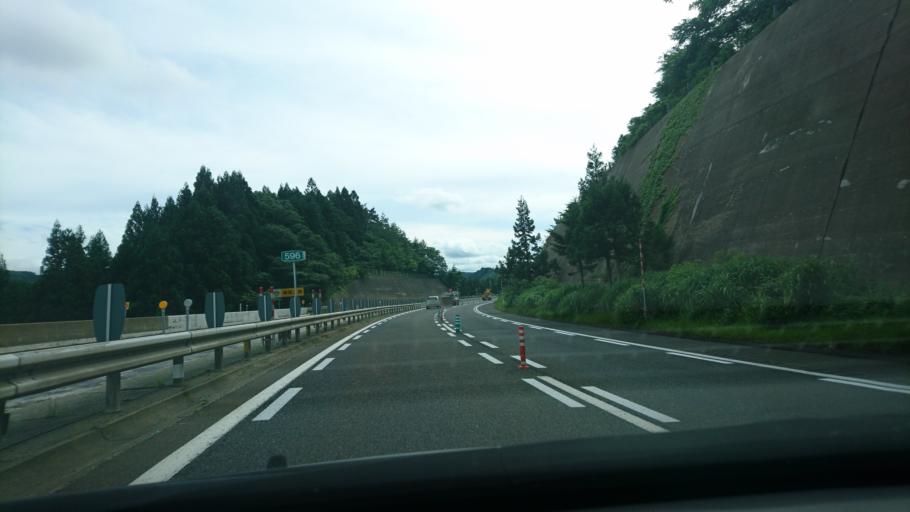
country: JP
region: Iwate
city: Ichinohe
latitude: 40.2222
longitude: 141.3604
